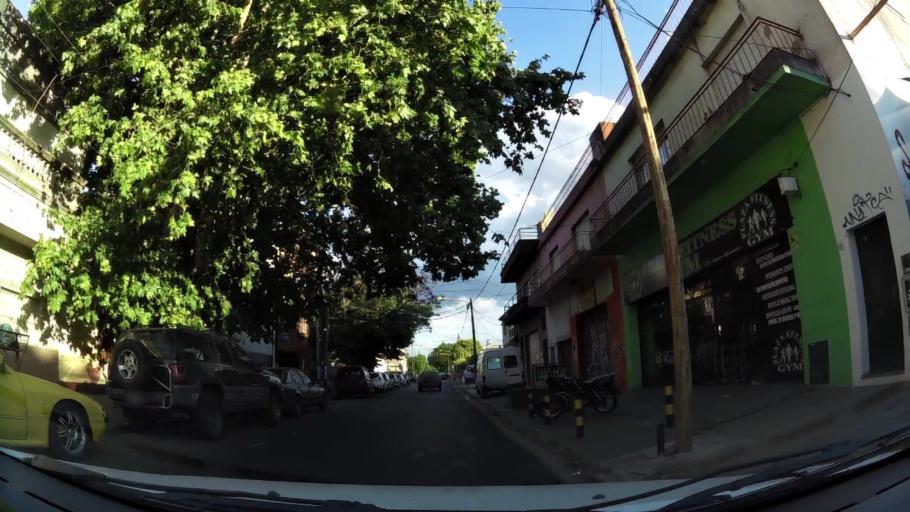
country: AR
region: Buenos Aires
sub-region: Partido de General San Martin
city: General San Martin
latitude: -34.5620
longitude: -58.5491
